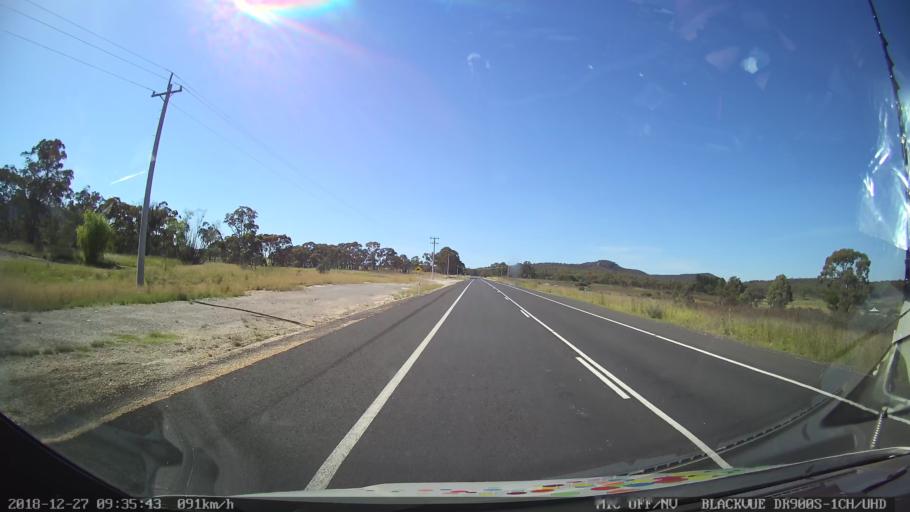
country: AU
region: New South Wales
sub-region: Lithgow
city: Portland
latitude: -33.2422
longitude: 150.0320
